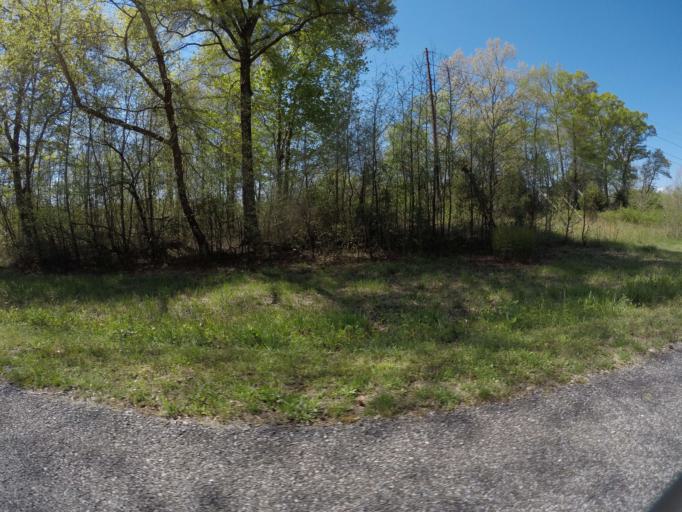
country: US
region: Maryland
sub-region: Charles County
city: Potomac Heights
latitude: 38.5933
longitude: -77.1178
